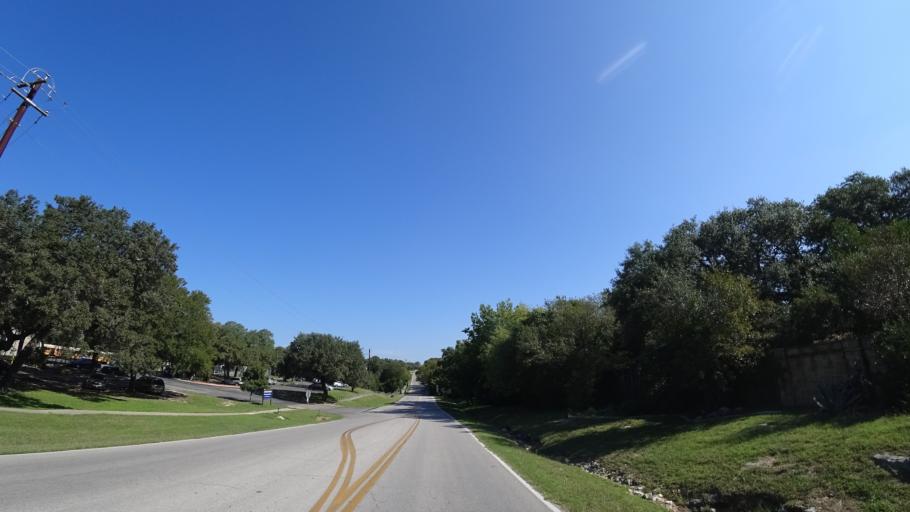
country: US
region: Texas
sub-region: Travis County
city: Rollingwood
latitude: 30.2753
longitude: -97.8104
